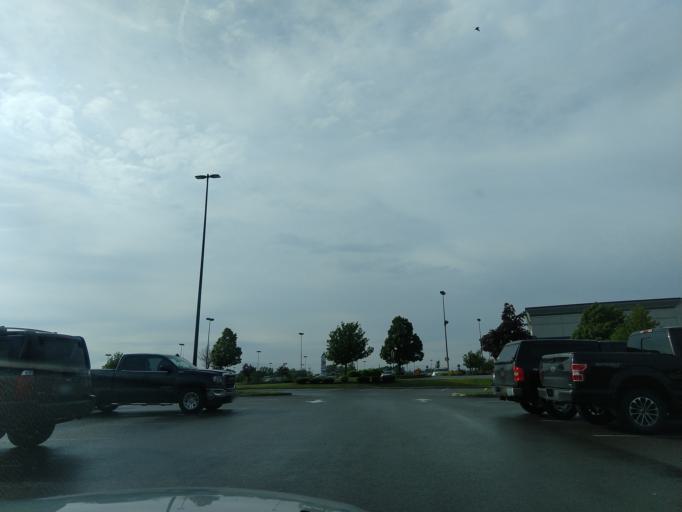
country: US
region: New York
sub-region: Erie County
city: Sloan
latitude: 42.9034
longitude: -78.7788
